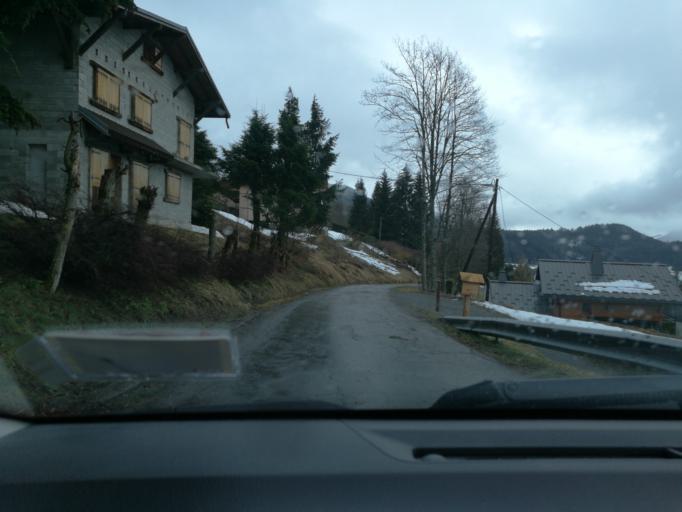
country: FR
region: Rhone-Alpes
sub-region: Departement de la Haute-Savoie
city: Araches-la-Frasse
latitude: 46.0538
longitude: 6.6346
